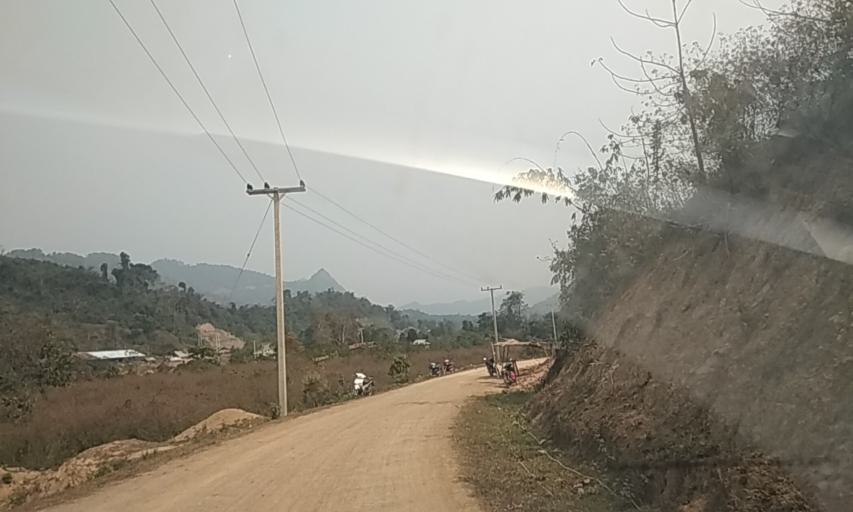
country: VN
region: Huyen Dien Bien
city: Dien Bien Phu
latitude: 21.4260
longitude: 102.7624
